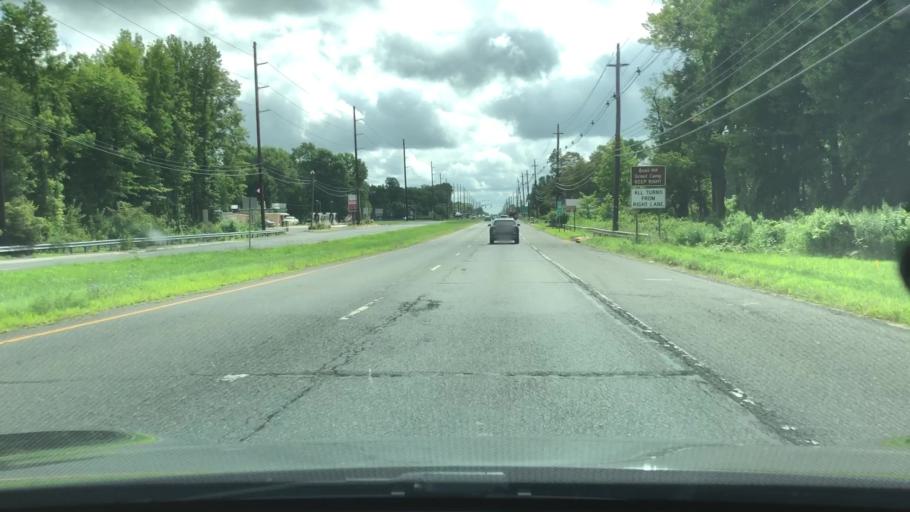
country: US
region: New Jersey
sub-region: Monmouth County
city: Englishtown
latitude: 40.2587
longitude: -74.3998
